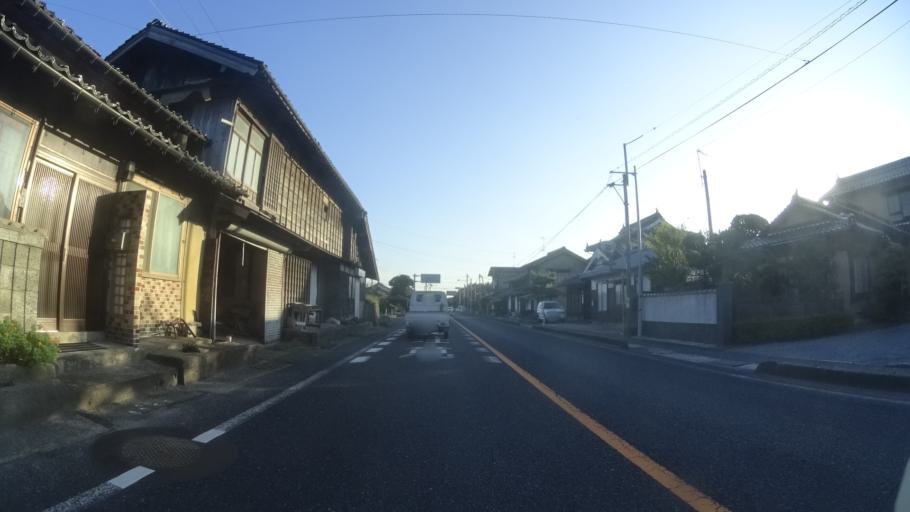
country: JP
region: Tottori
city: Yonago
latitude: 35.4862
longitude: 133.4441
